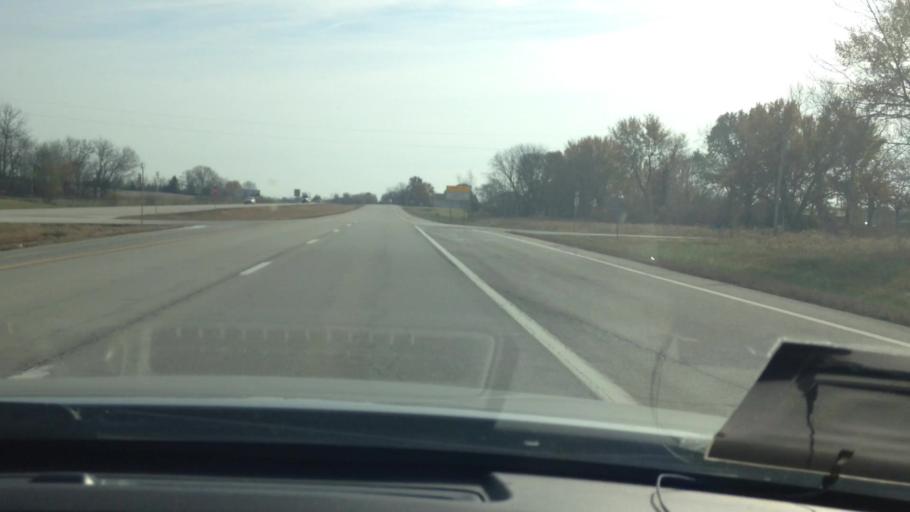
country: US
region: Missouri
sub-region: Cass County
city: Harrisonville
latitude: 38.6158
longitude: -94.3300
